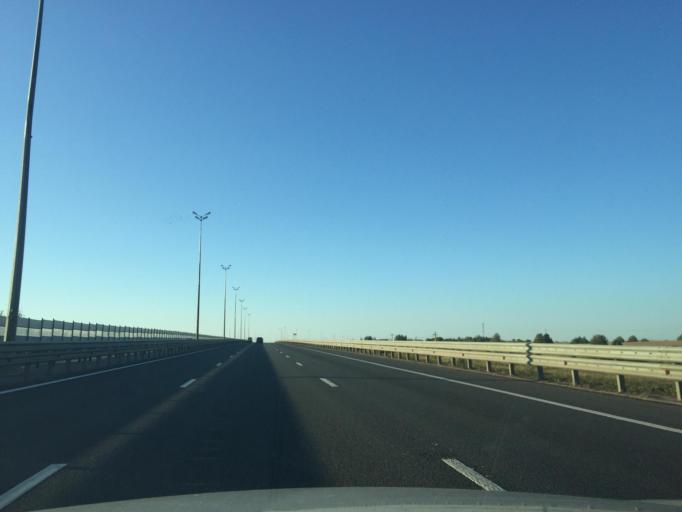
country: RU
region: Leningrad
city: Maloye Verevo
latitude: 59.6612
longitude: 30.2297
